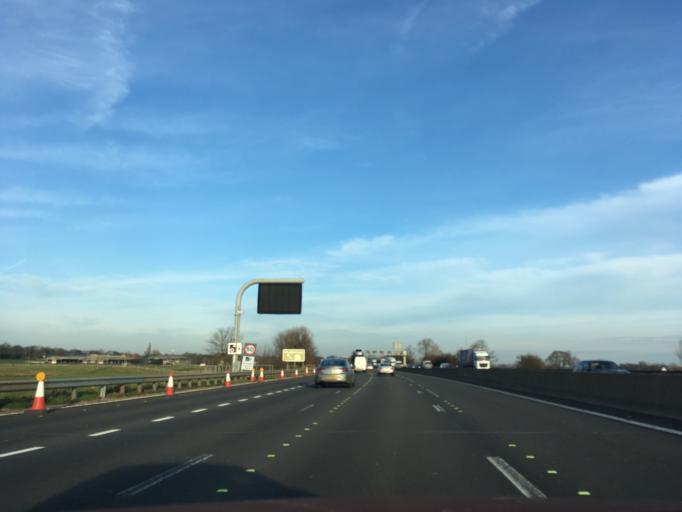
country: GB
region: England
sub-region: Staffordshire
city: Penkridge
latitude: 52.7553
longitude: -2.1015
